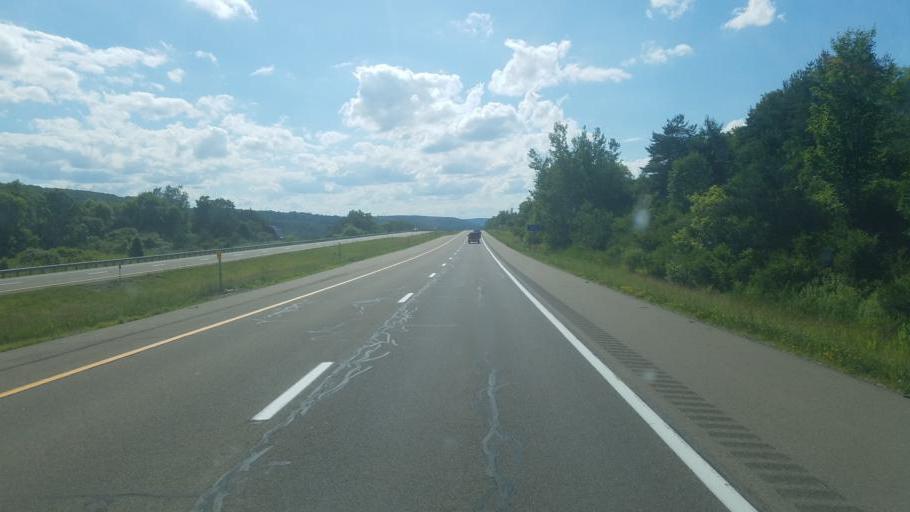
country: US
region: New York
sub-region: Steuben County
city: Hornell
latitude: 42.3675
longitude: -77.6004
